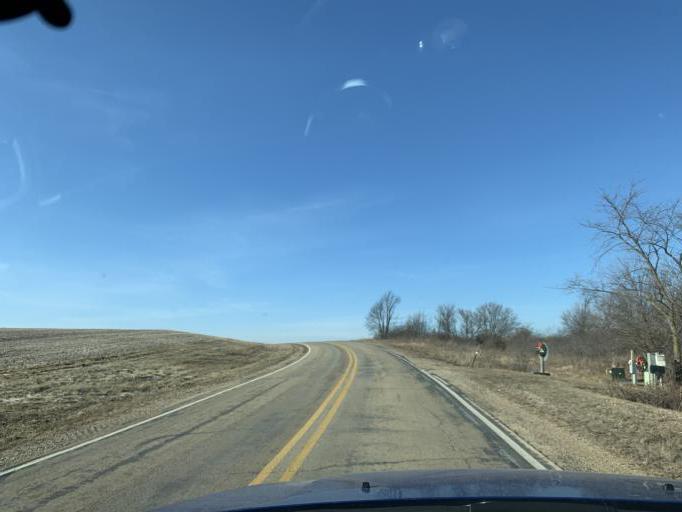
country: US
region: Wisconsin
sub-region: Iowa County
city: Barneveld
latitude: 42.8089
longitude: -89.8844
